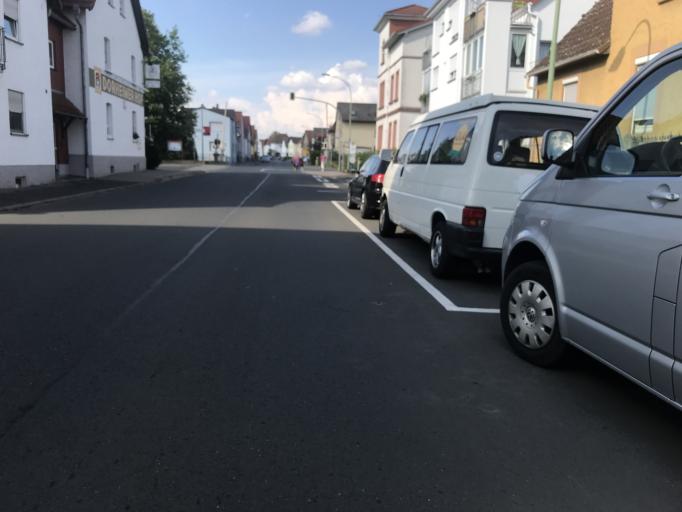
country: DE
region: Hesse
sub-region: Regierungsbezirk Darmstadt
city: Friedberg
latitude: 50.3519
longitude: 8.7916
